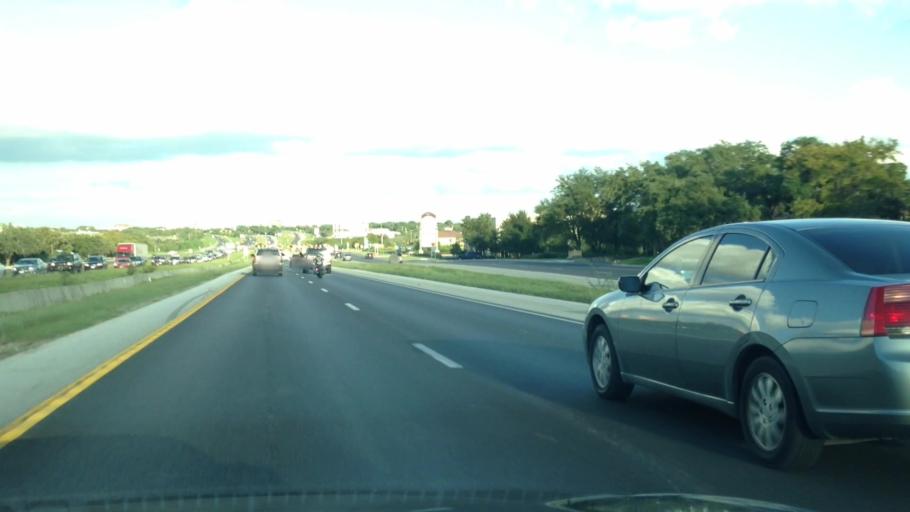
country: US
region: Texas
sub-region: Bexar County
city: Shavano Park
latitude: 29.6010
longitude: -98.5504
